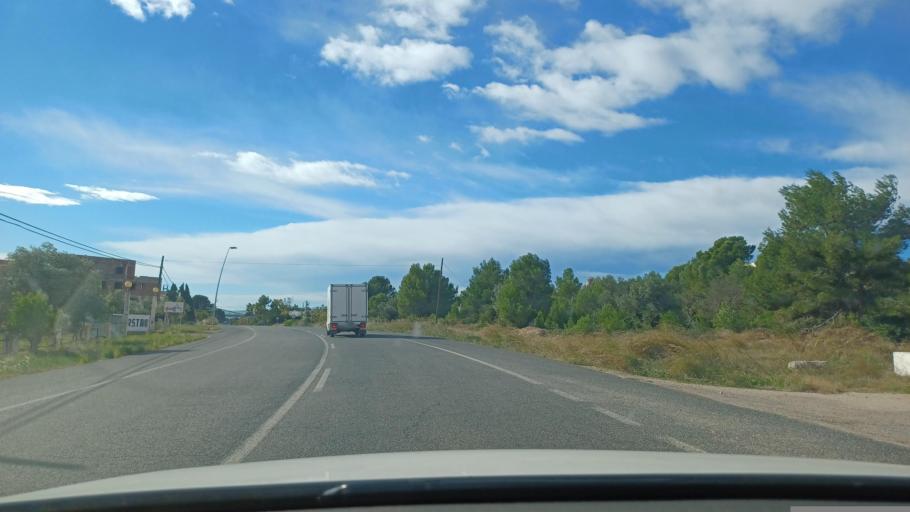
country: ES
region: Catalonia
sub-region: Provincia de Tarragona
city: Sant Carles de la Rapita
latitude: 40.5856
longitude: 0.5577
